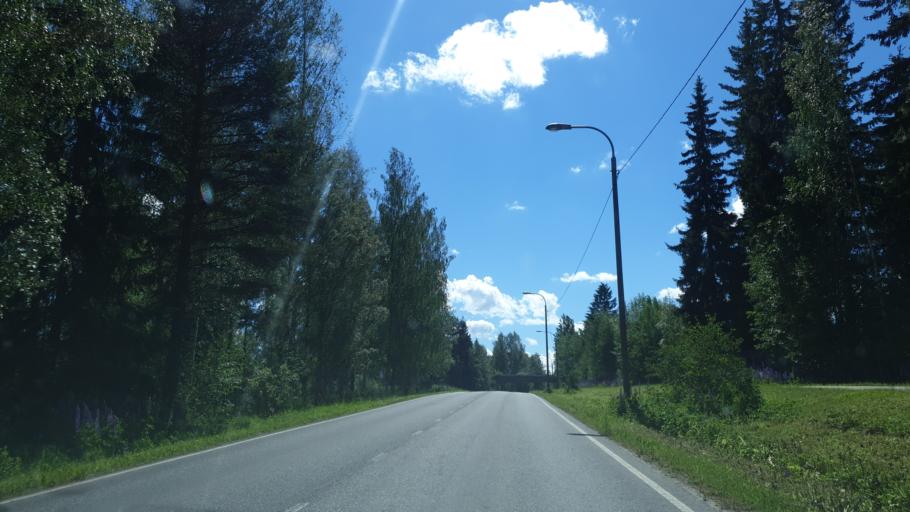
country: FI
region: Northern Savo
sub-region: Koillis-Savo
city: Kaavi
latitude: 62.9833
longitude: 28.5010
